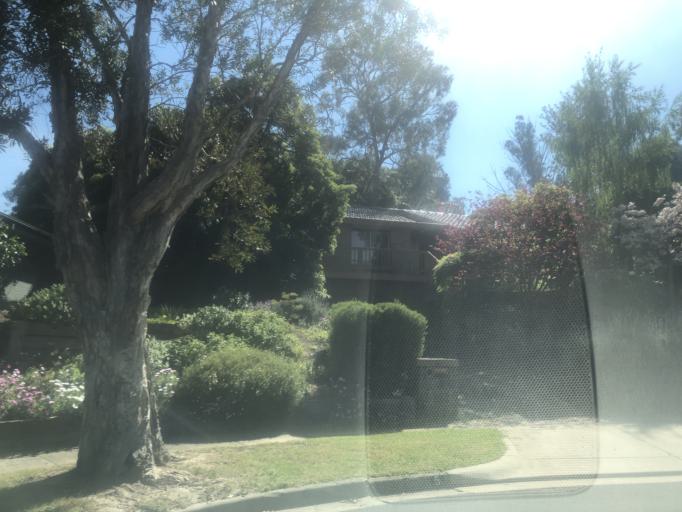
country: AU
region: Victoria
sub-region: Monash
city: Mulgrave
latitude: -37.9020
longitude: 145.1888
